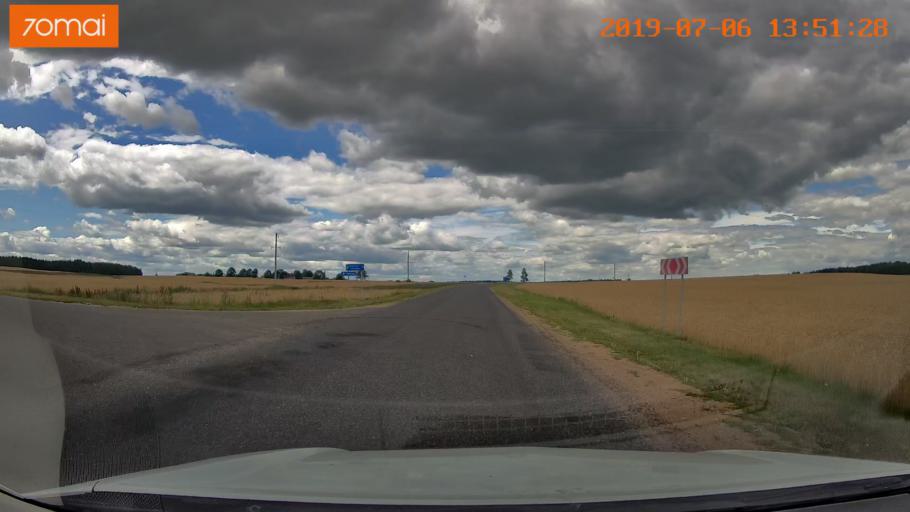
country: BY
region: Minsk
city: Ivyanyets
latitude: 53.7085
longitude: 26.8313
